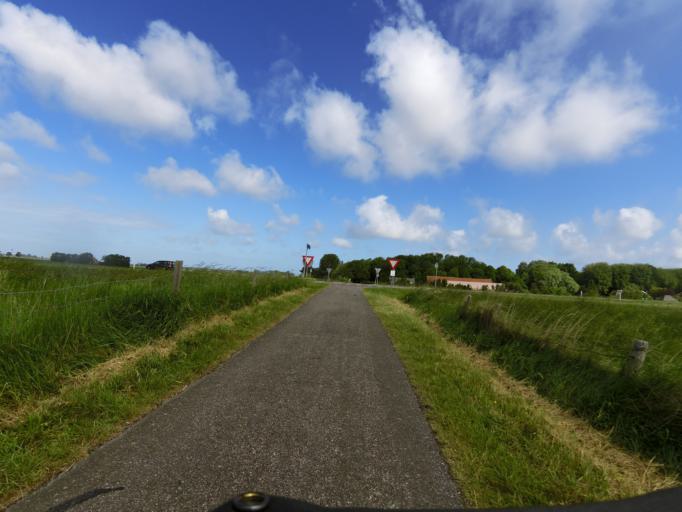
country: NL
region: Zeeland
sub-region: Schouwen-Duiveland
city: Scharendijke
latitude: 51.6715
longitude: 3.9421
